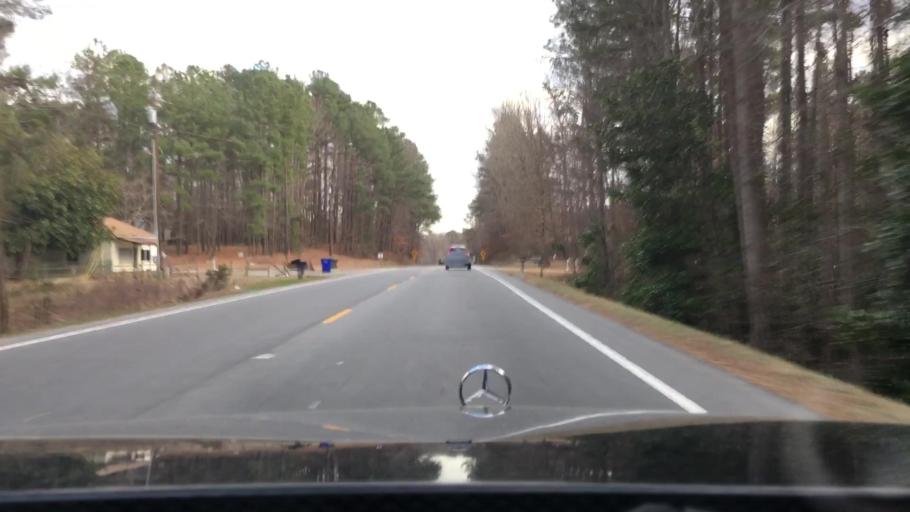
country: US
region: North Carolina
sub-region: Orange County
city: Hillsborough
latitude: 36.0593
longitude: -79.0531
